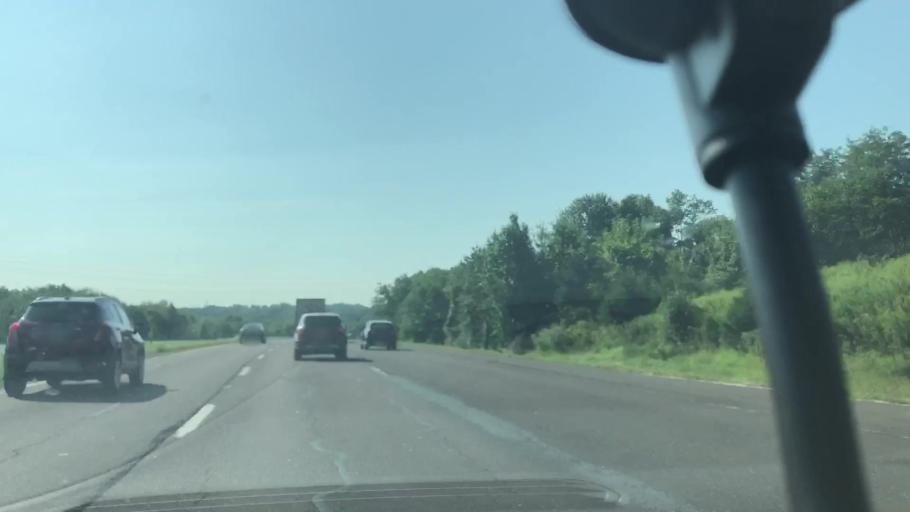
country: US
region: Pennsylvania
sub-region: Montgomery County
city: Royersford
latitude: 40.1926
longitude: -75.5219
